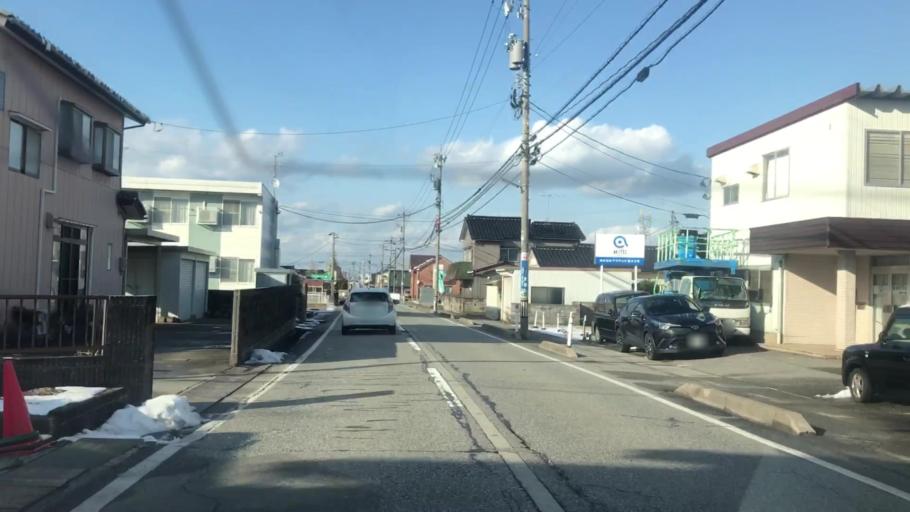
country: JP
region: Toyama
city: Toyama-shi
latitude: 36.6772
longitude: 137.2738
